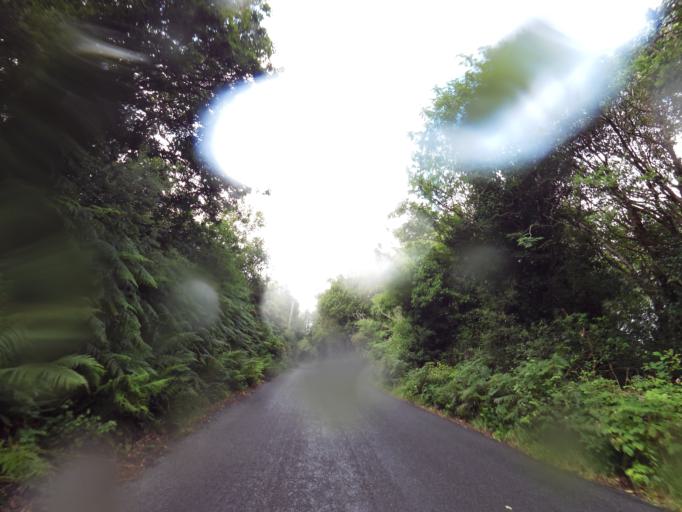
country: IE
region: Connaught
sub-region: County Galway
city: Oughterard
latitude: 53.4079
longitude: -9.3281
